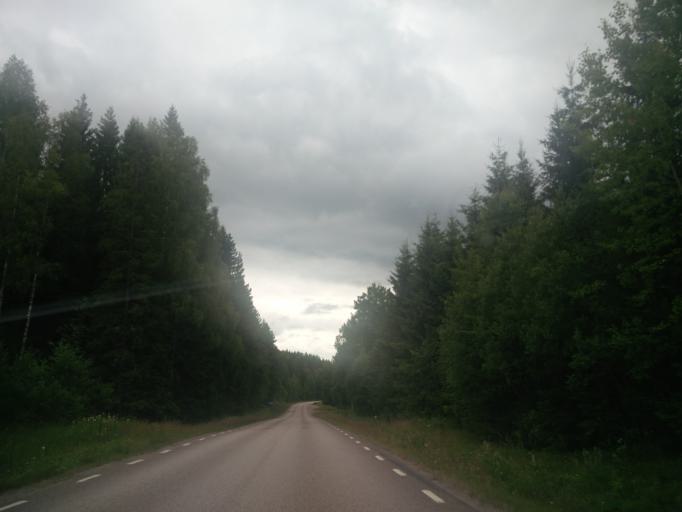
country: SE
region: Vaermland
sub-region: Arvika Kommun
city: Arvika
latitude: 59.9287
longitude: 12.6612
